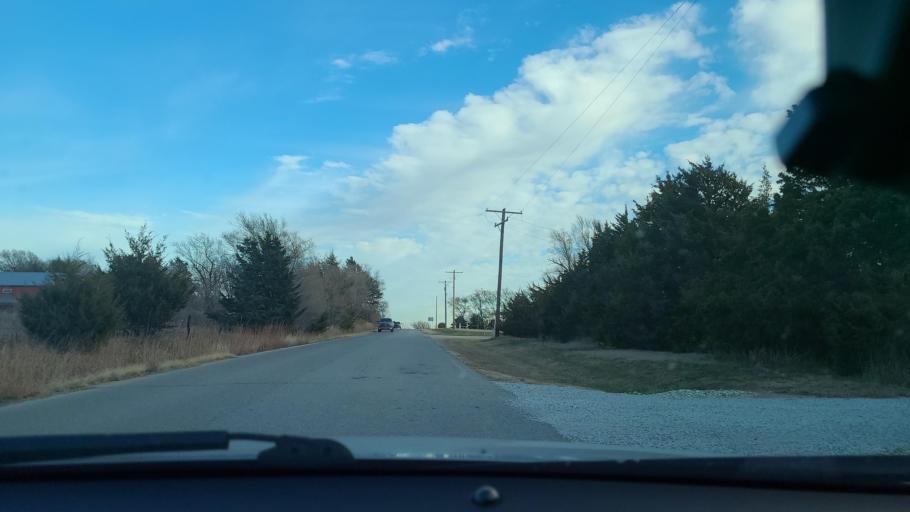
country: US
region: Kansas
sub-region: Sedgwick County
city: Goddard
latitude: 37.6496
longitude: -97.5829
